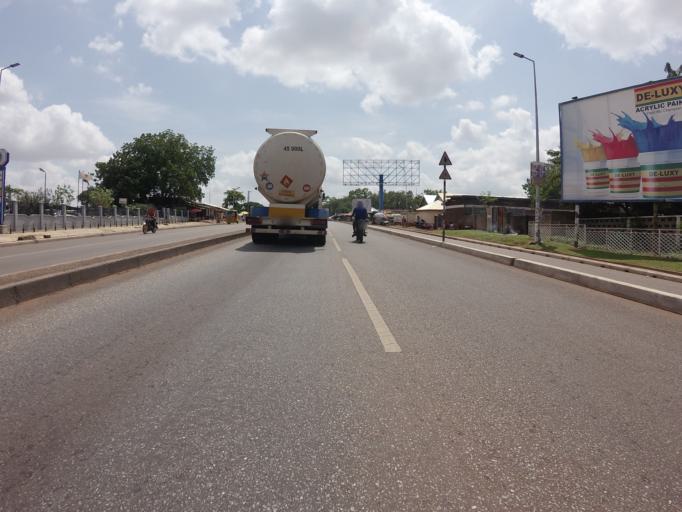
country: GH
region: Northern
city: Tamale
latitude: 9.4009
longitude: -0.8358
